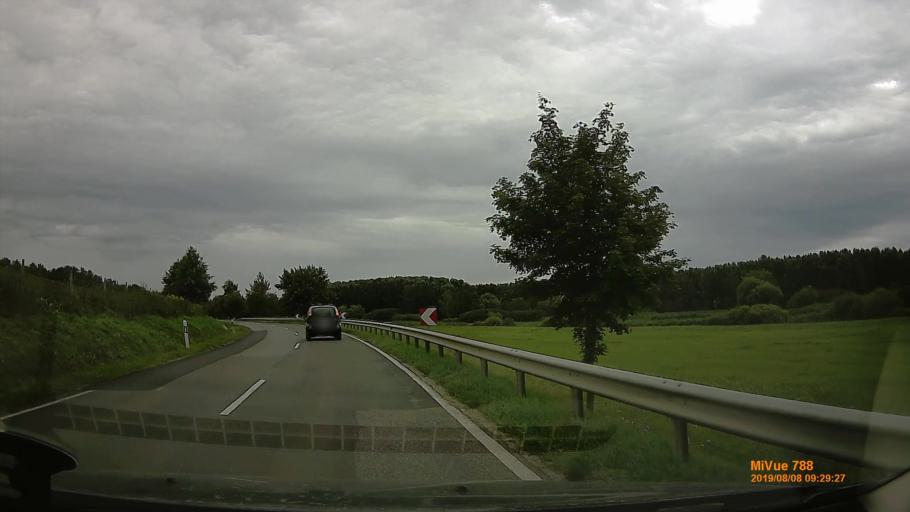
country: HU
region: Vas
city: Vasvar
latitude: 46.9754
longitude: 16.8431
